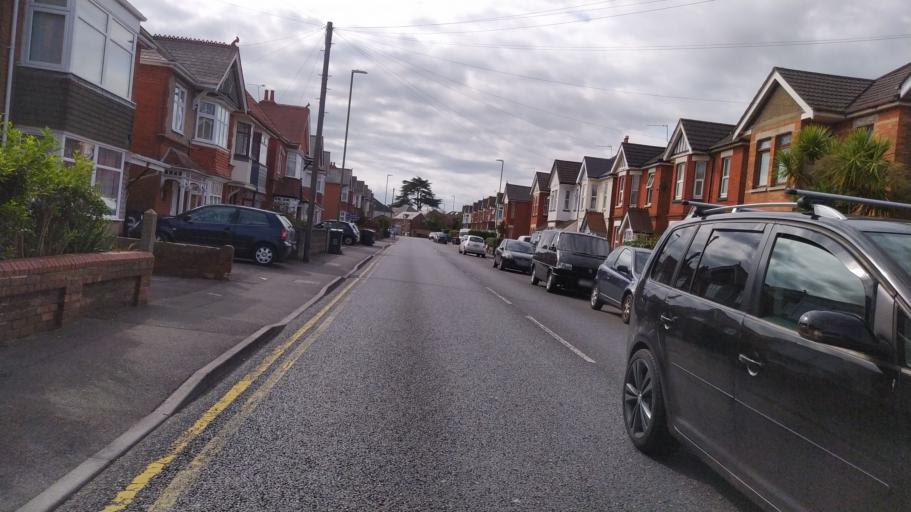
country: GB
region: England
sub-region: Bournemouth
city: Bournemouth
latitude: 50.7459
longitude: -1.8847
